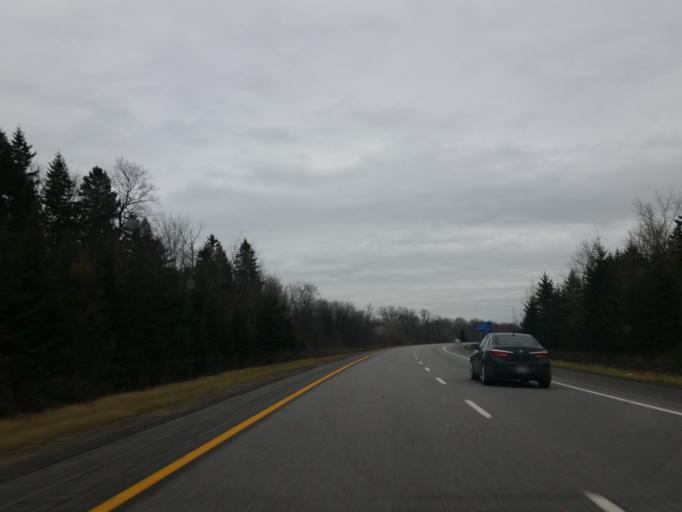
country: CA
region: Quebec
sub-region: Capitale-Nationale
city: Saint-Marc-des-Carrieres
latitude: 46.6554
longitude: -71.9739
